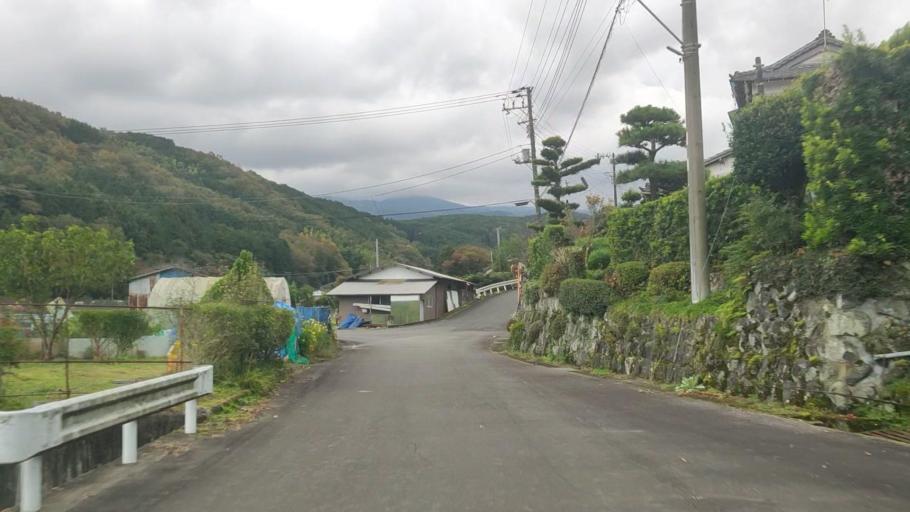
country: JP
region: Shizuoka
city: Ito
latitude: 34.9297
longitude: 138.9898
